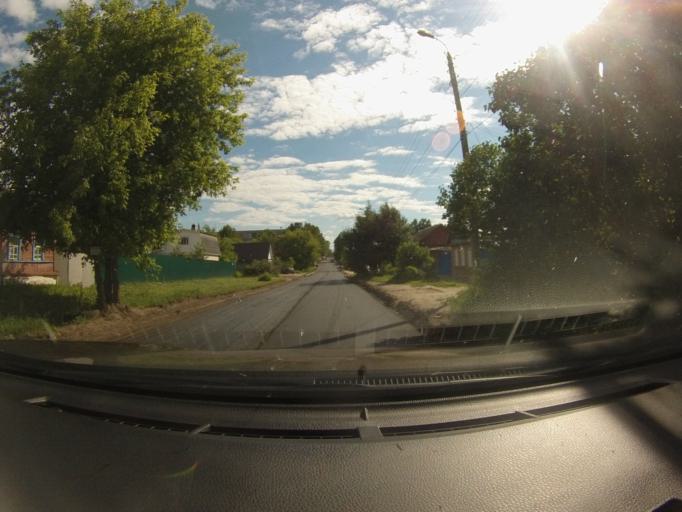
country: RU
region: Orjol
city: Mtsensk
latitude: 53.2855
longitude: 36.5792
